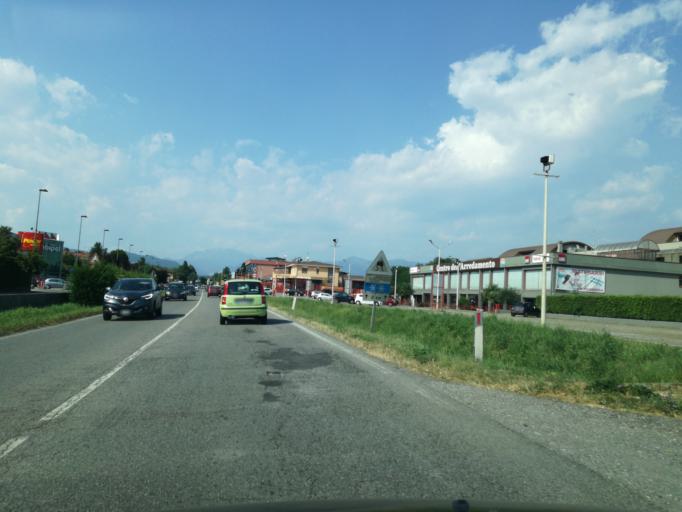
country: IT
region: Lombardy
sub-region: Provincia di Lecco
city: Osnago
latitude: 45.6760
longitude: 9.3957
